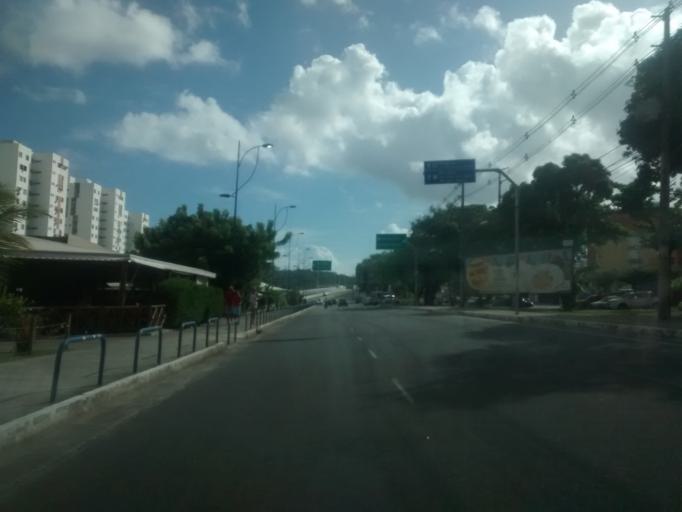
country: BR
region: Bahia
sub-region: Salvador
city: Salvador
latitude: -12.9691
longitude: -38.4358
